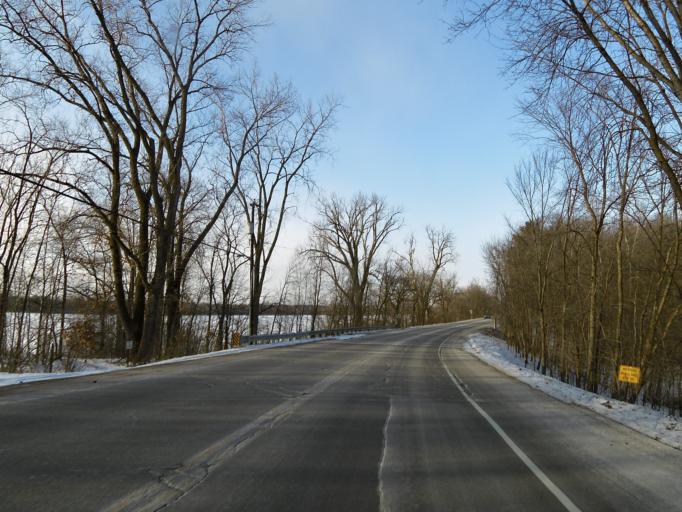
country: US
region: Minnesota
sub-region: Washington County
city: Lake Elmo
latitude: 44.9758
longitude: -92.8834
